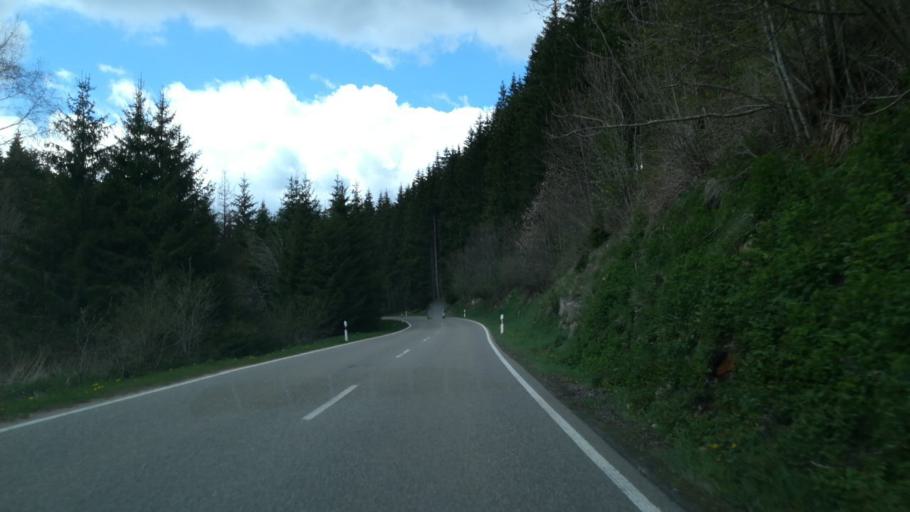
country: DE
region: Baden-Wuerttemberg
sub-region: Freiburg Region
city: Schluchsee
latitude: 47.7991
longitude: 8.2070
